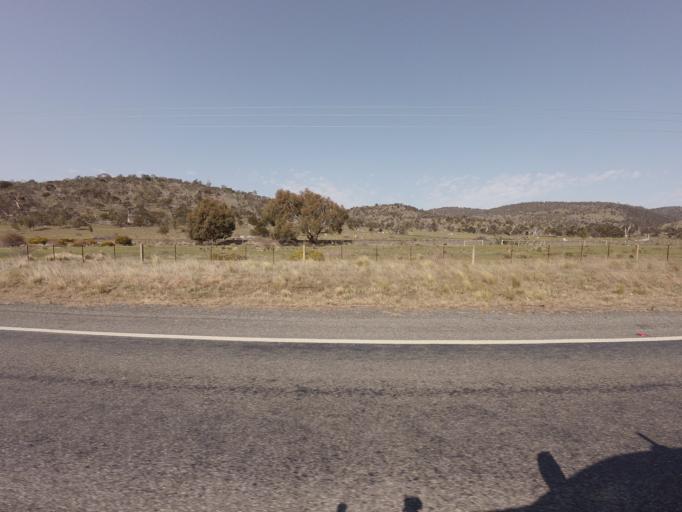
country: AU
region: Tasmania
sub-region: Northern Midlands
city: Evandale
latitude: -41.8118
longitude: 147.5874
